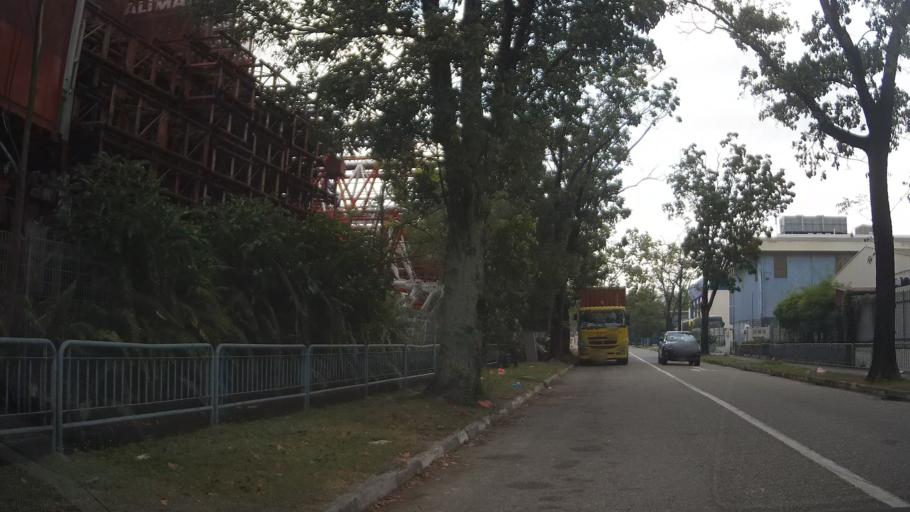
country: MY
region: Johor
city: Johor Bahru
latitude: 1.3183
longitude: 103.6450
